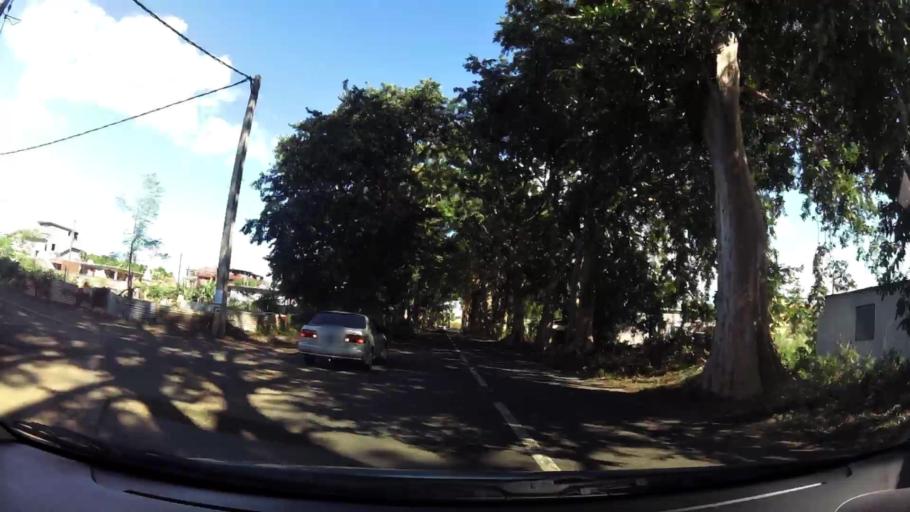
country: MU
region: Grand Port
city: Mahebourg
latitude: -20.4092
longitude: 57.6939
